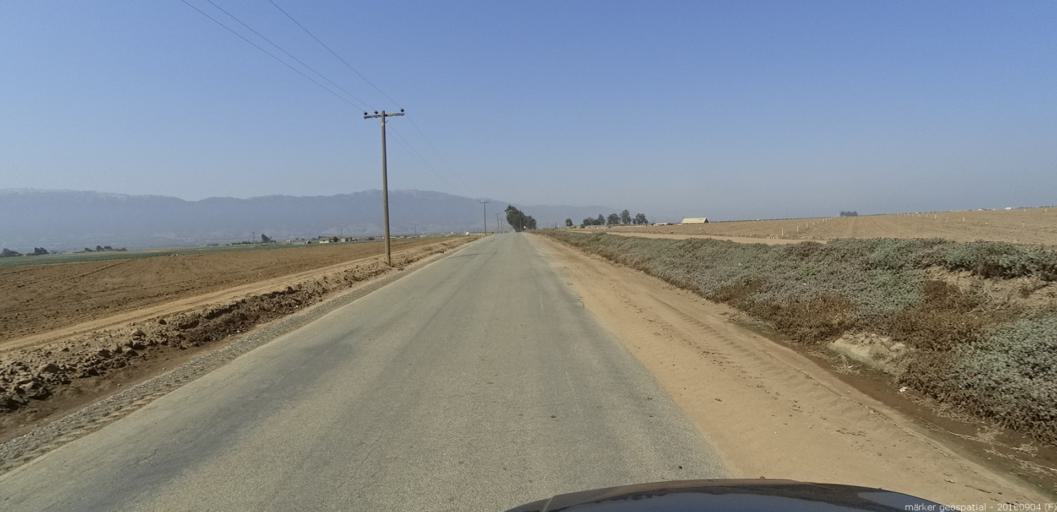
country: US
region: California
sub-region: Monterey County
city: Gonzales
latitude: 36.5573
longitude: -121.4639
